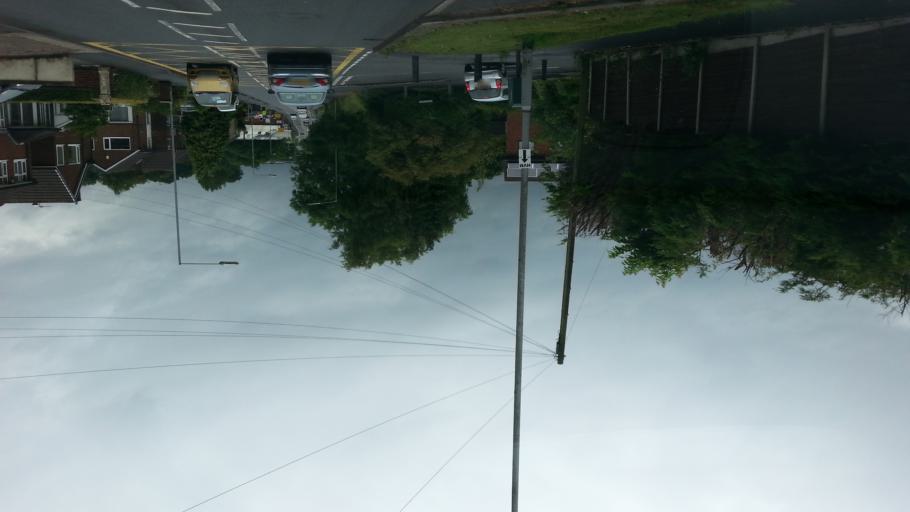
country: GB
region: England
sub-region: Borough of Bury
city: Whitefield
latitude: 53.5702
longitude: -2.2871
